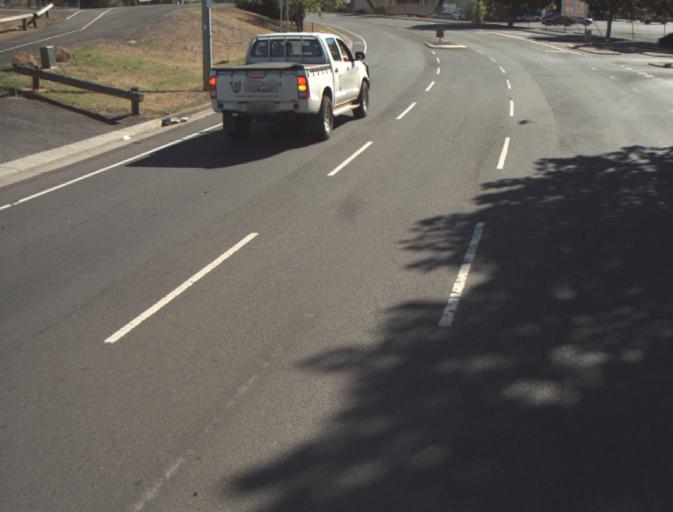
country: AU
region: Tasmania
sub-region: Launceston
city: Launceston
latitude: -41.4304
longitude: 147.1424
